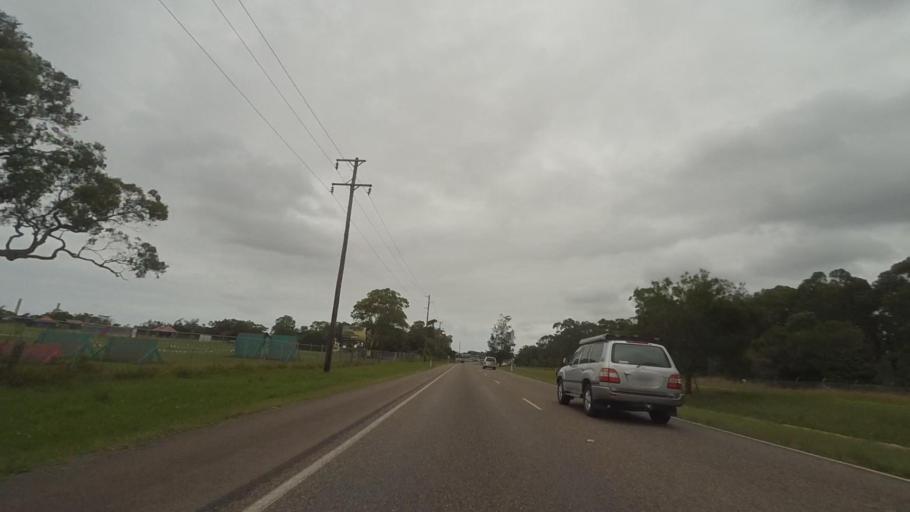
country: AU
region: New South Wales
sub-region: Wyong Shire
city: Buff Point
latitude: -33.1927
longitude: 151.5273
